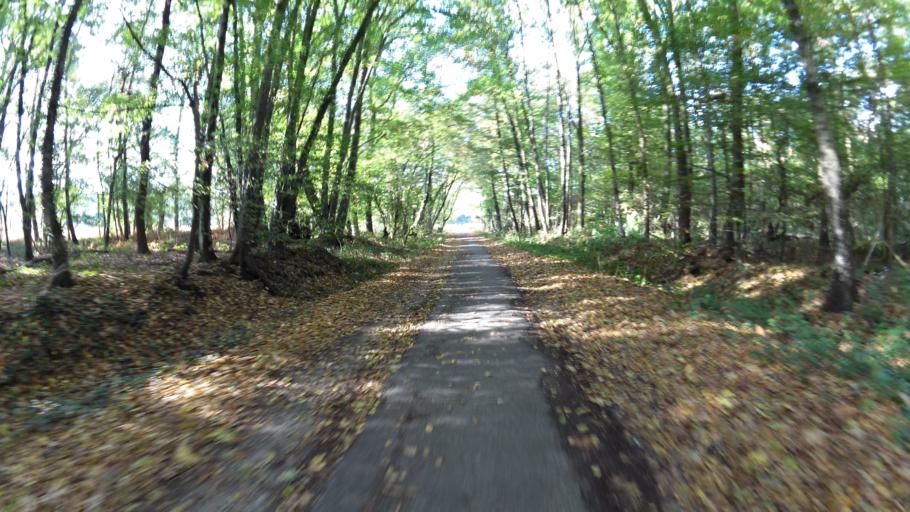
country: NL
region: Limburg
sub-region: Gemeente Heerlen
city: Heerlen
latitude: 50.9193
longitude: 6.0075
